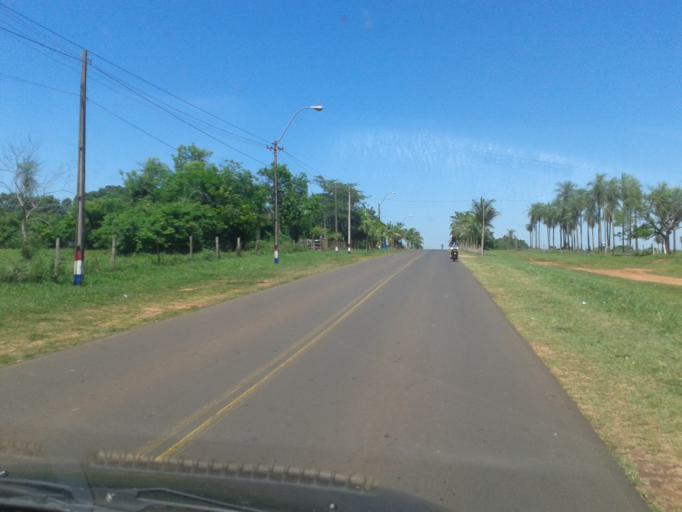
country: PY
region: Misiones
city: Santa Rosa
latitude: -26.8887
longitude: -56.8620
